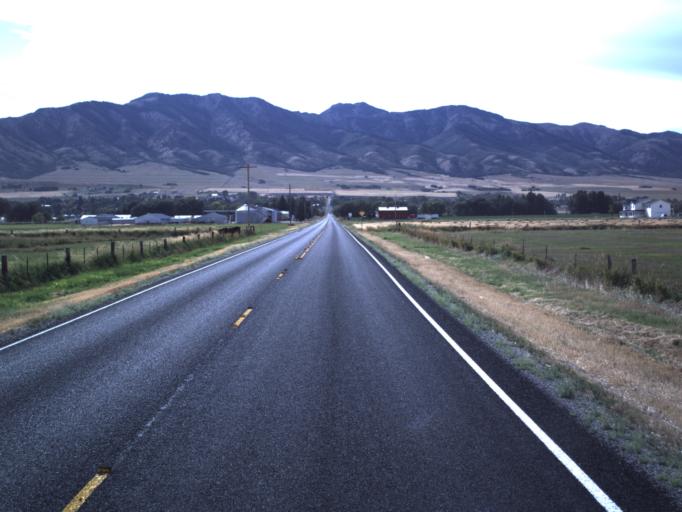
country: US
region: Utah
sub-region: Cache County
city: Benson
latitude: 41.9196
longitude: -112.0272
